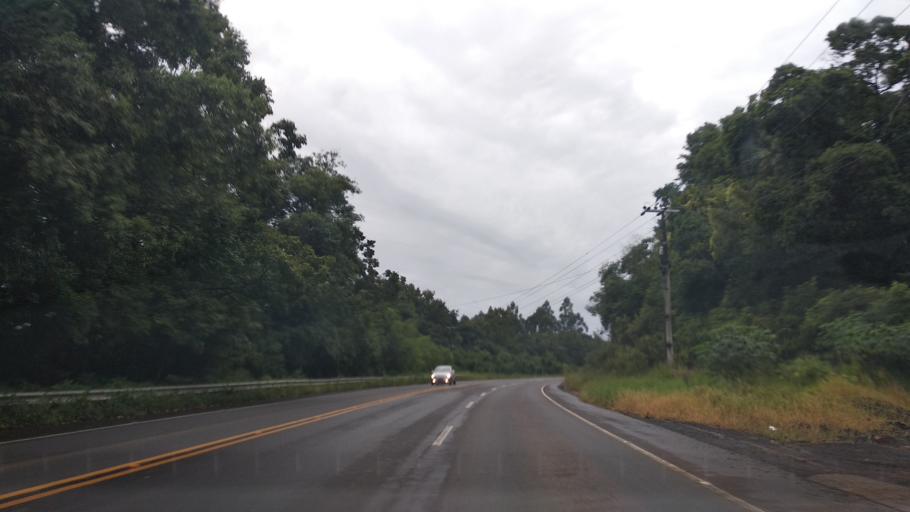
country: BR
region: Santa Catarina
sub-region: Videira
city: Videira
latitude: -27.0711
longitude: -51.2353
